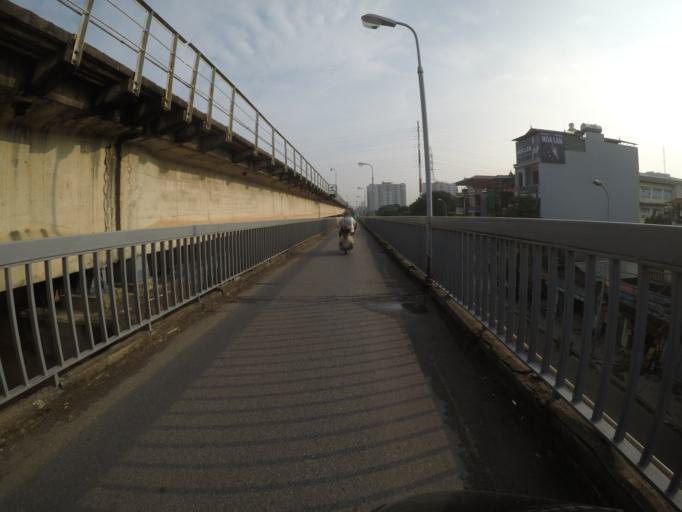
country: VN
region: Ha Noi
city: Tay Ho
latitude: 21.0888
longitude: 105.7857
